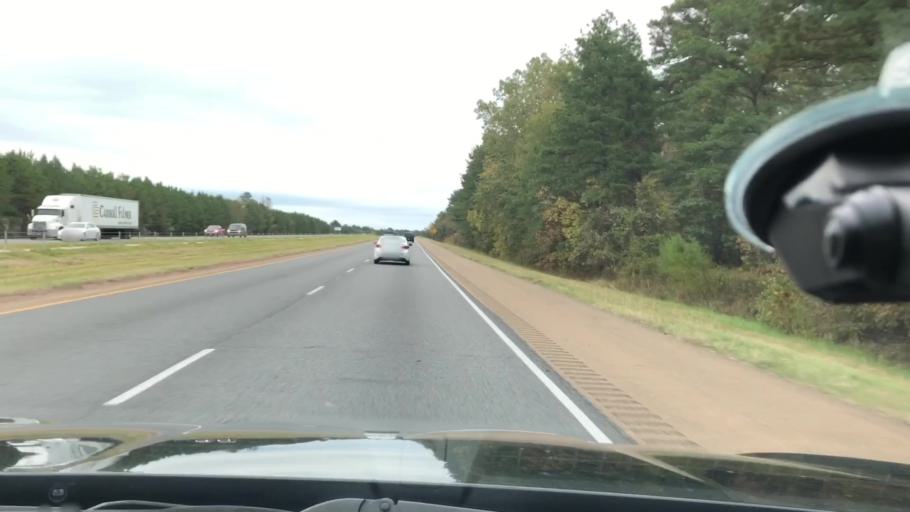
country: US
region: Arkansas
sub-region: Clark County
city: Gurdon
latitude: 33.9473
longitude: -93.2374
